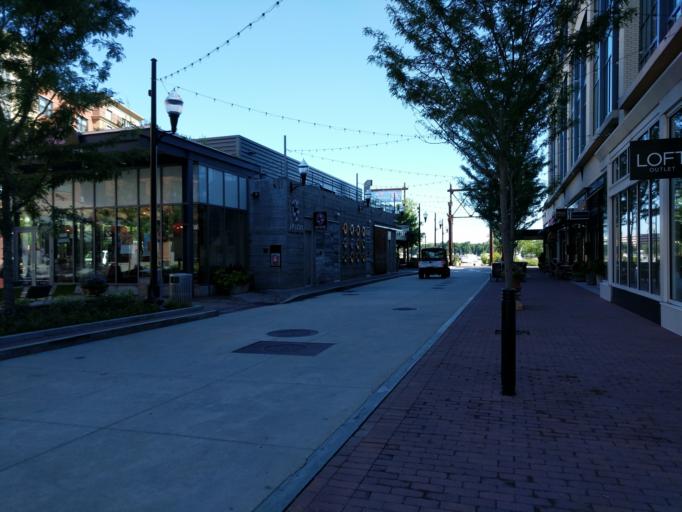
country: US
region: Massachusetts
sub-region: Middlesex County
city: Somerville
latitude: 42.3951
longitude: -71.0795
